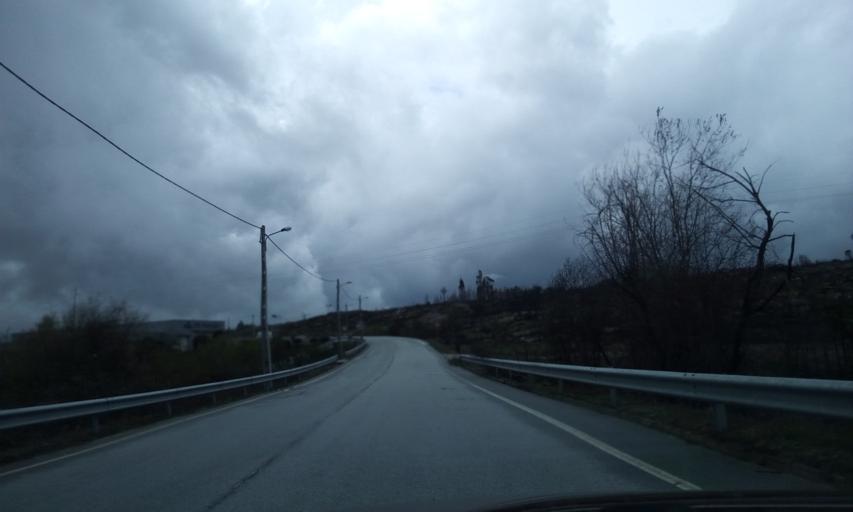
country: PT
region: Viseu
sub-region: Mangualde
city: Mangualde
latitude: 40.6016
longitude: -7.7978
